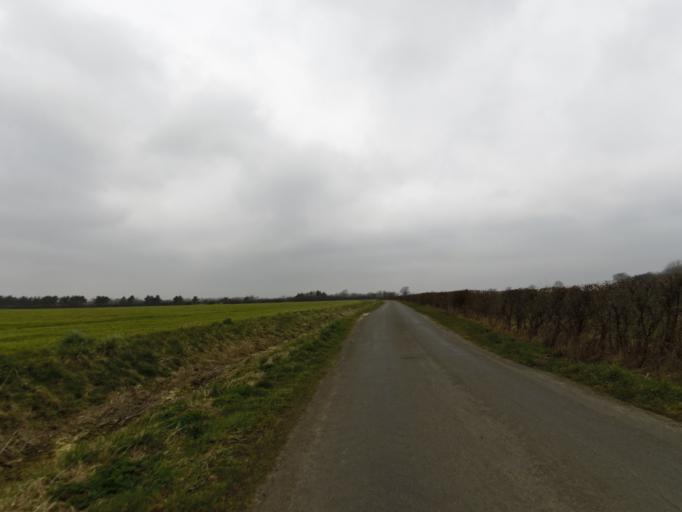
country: GB
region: England
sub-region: Suffolk
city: Framlingham
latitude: 52.2332
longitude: 1.3805
